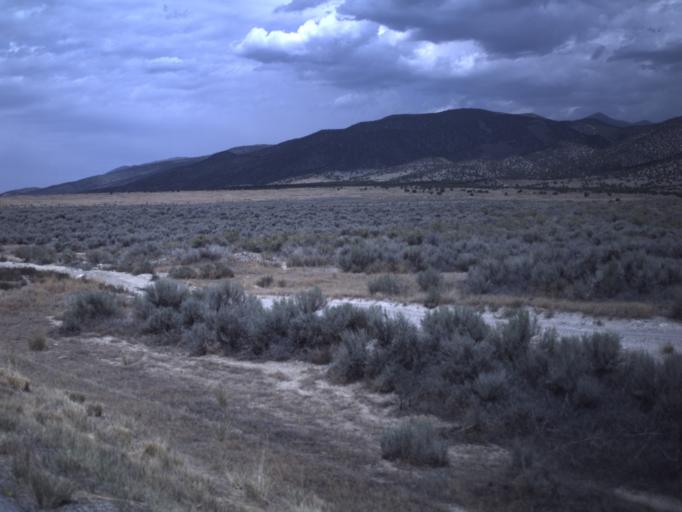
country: US
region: Utah
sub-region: Utah County
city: Eagle Mountain
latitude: 40.2489
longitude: -112.2158
